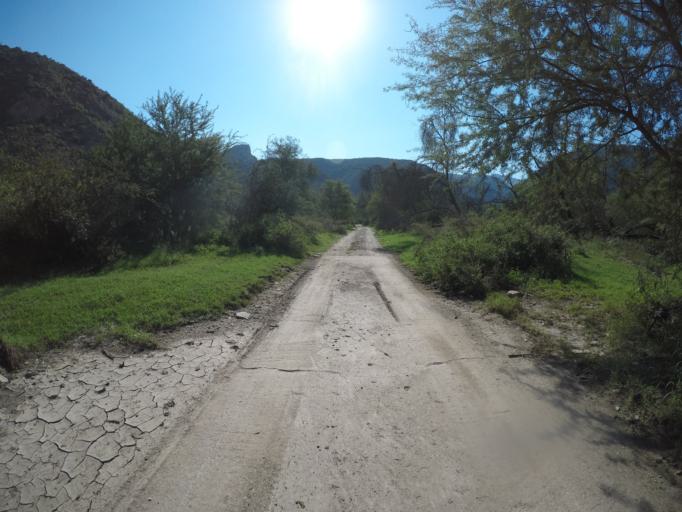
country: ZA
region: Eastern Cape
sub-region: Cacadu District Municipality
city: Kareedouw
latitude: -33.6574
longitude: 24.3660
